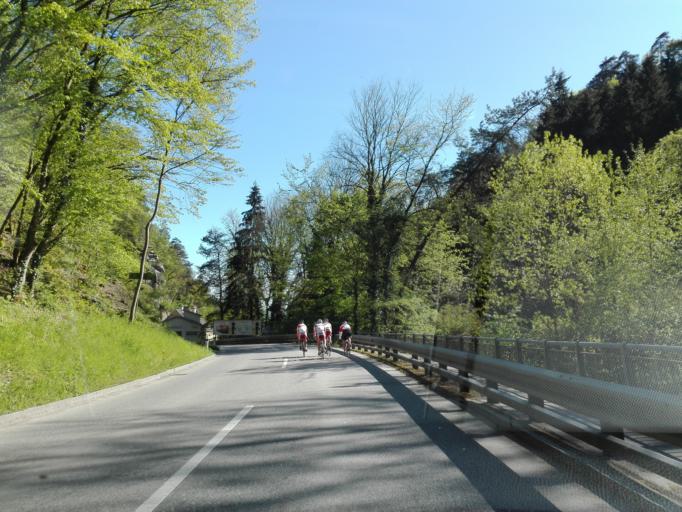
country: AT
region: Upper Austria
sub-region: Politischer Bezirk Perg
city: Perg
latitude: 48.2572
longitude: 14.6368
